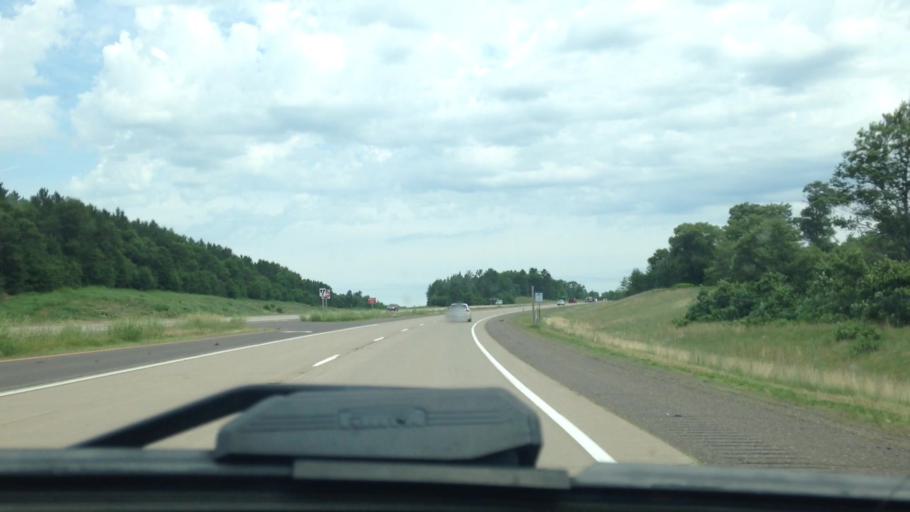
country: US
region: Wisconsin
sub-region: Douglas County
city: Lake Nebagamon
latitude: 46.2028
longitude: -91.7995
